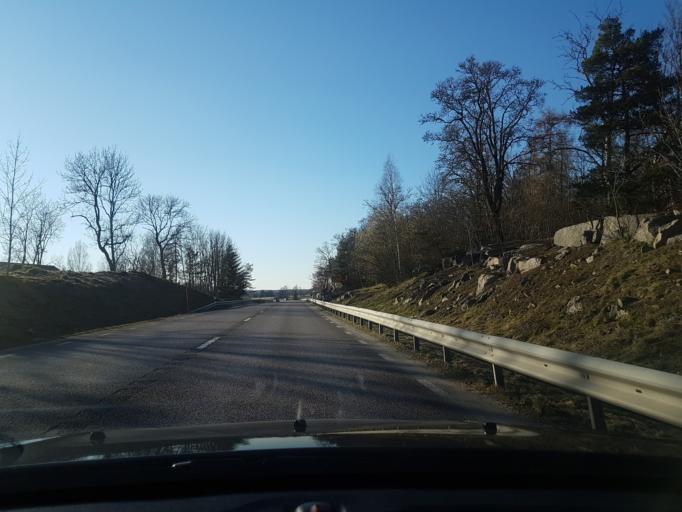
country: SE
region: Uppsala
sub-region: Enkopings Kommun
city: Orsundsbro
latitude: 59.8753
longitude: 17.2914
